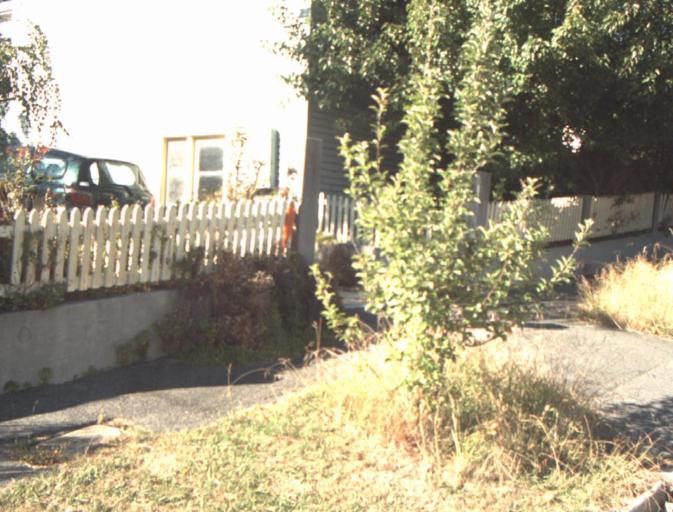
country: AU
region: Tasmania
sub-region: Launceston
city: East Launceston
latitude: -41.4578
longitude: 147.1499
